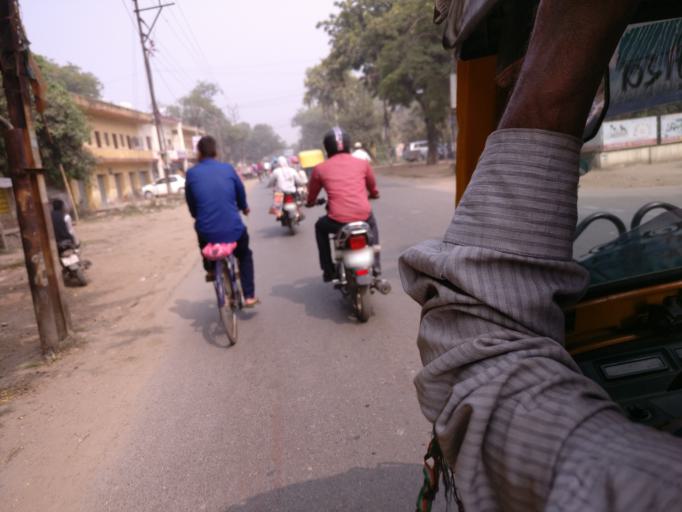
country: IN
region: Uttar Pradesh
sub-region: Varanasi
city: Varanasi
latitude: 25.2803
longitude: 82.9674
